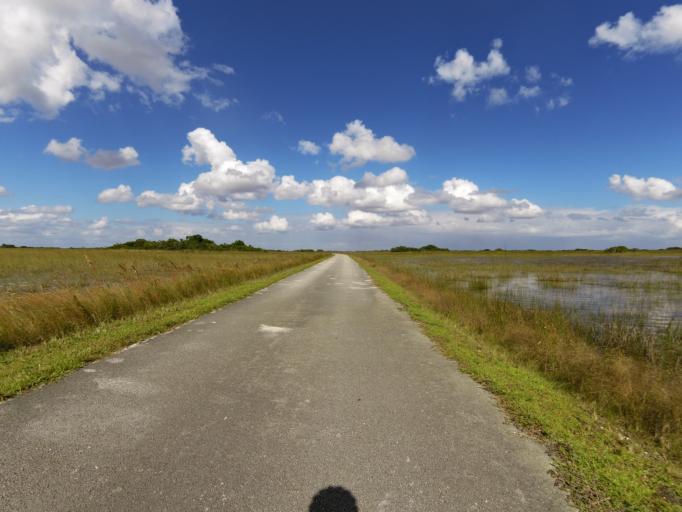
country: US
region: Florida
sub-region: Miami-Dade County
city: The Hammocks
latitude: 25.6886
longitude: -80.7610
